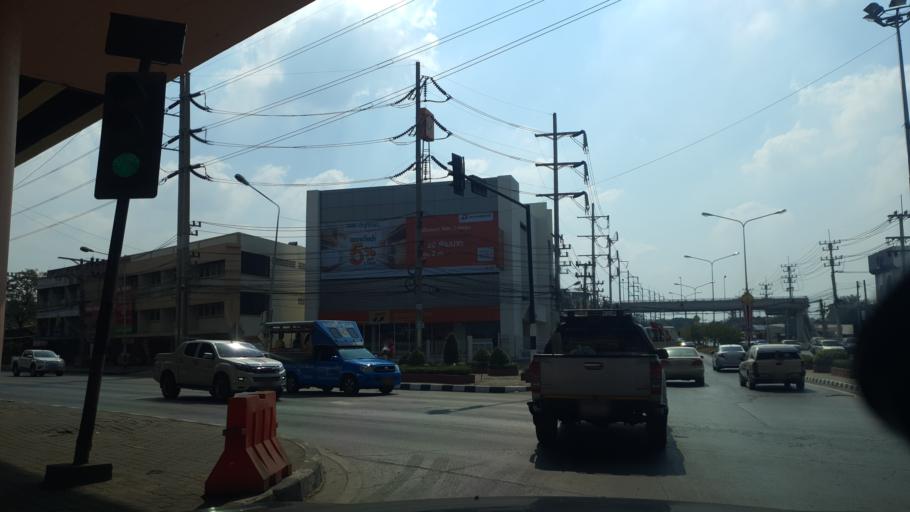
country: TH
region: Bangkok
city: Nong Khaem
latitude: 13.7065
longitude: 100.2990
